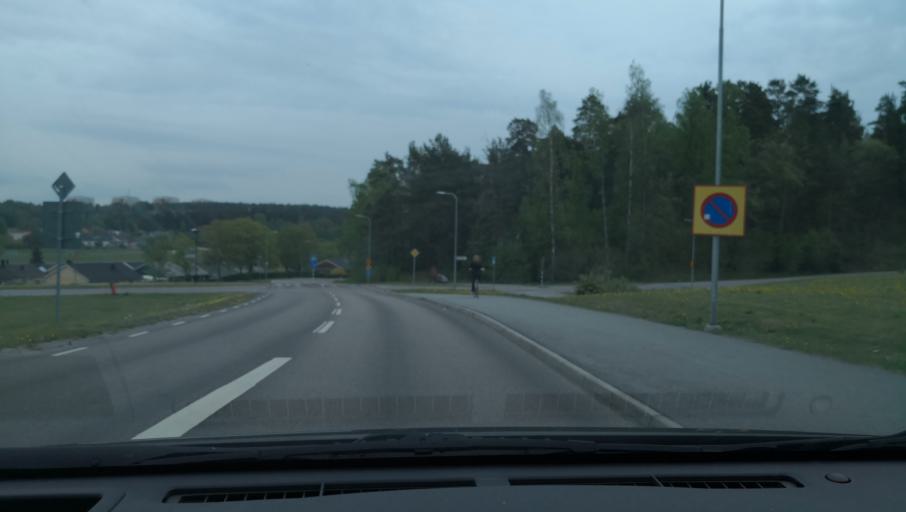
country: SE
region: Stockholm
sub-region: Upplands-Bro Kommun
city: Kungsaengen
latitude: 59.4916
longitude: 17.7378
